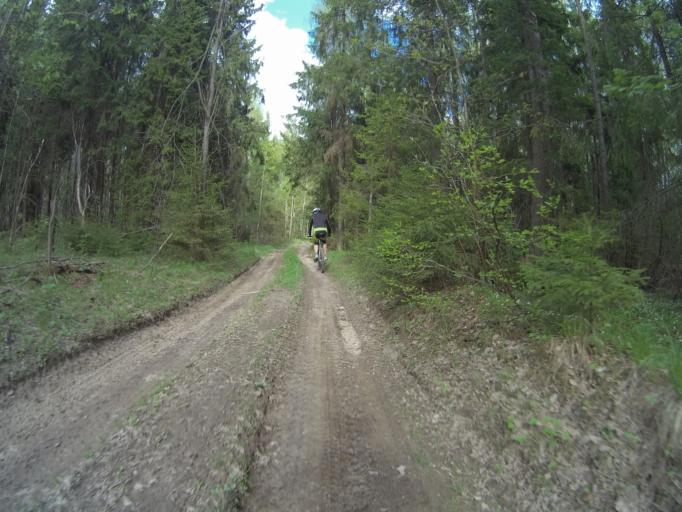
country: RU
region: Vladimir
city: Orgtrud
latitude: 56.1063
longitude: 40.6780
